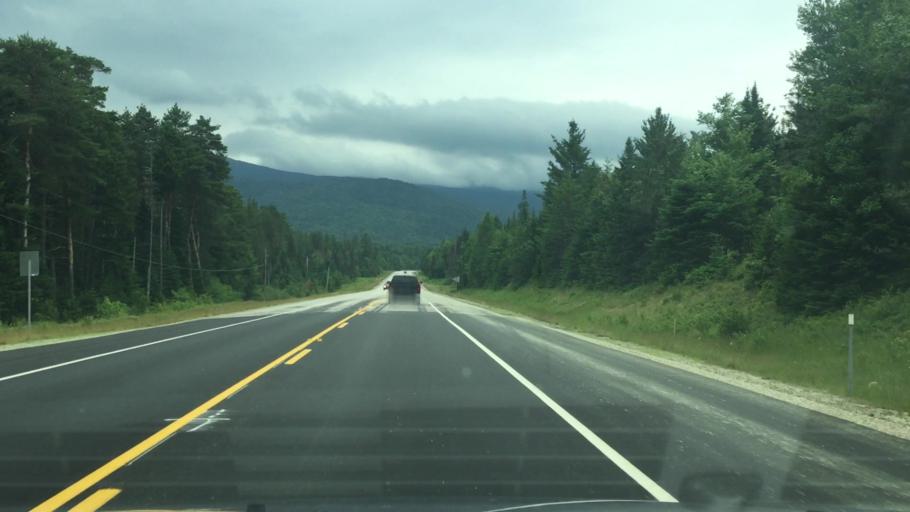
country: US
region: New Hampshire
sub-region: Coos County
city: Jefferson
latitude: 44.2482
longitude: -71.4384
